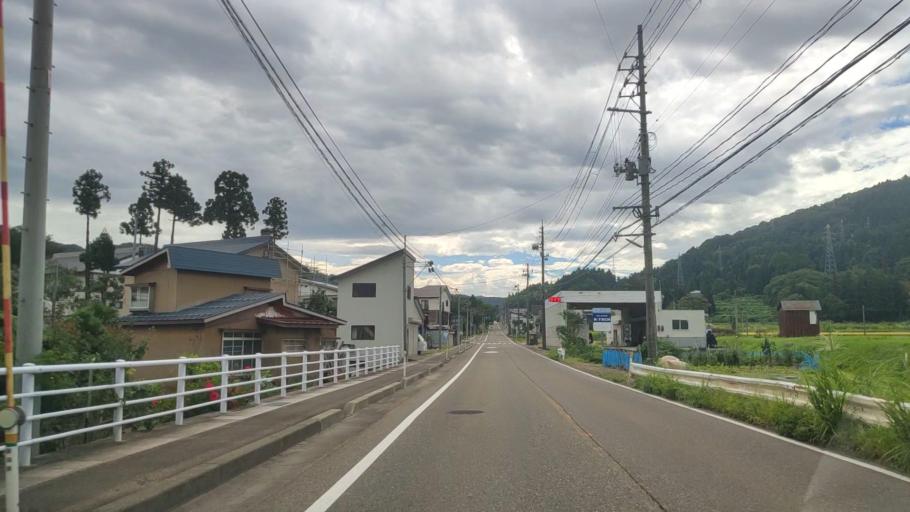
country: JP
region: Niigata
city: Arai
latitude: 37.0028
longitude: 138.2636
